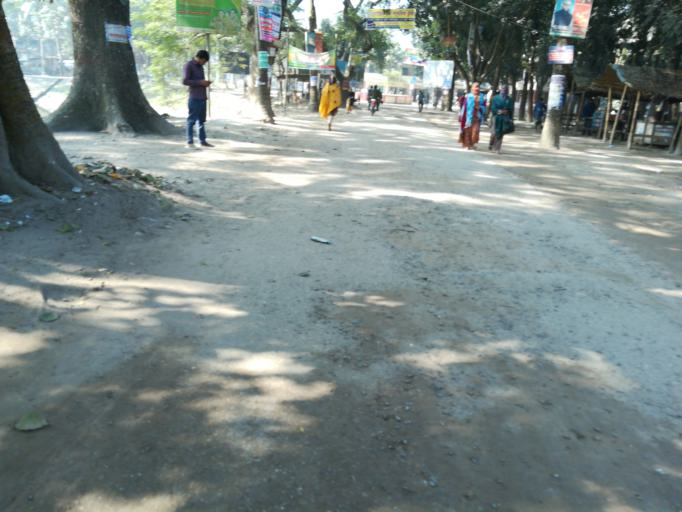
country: BD
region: Rangpur Division
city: Rangpur
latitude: 25.5700
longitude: 89.2740
